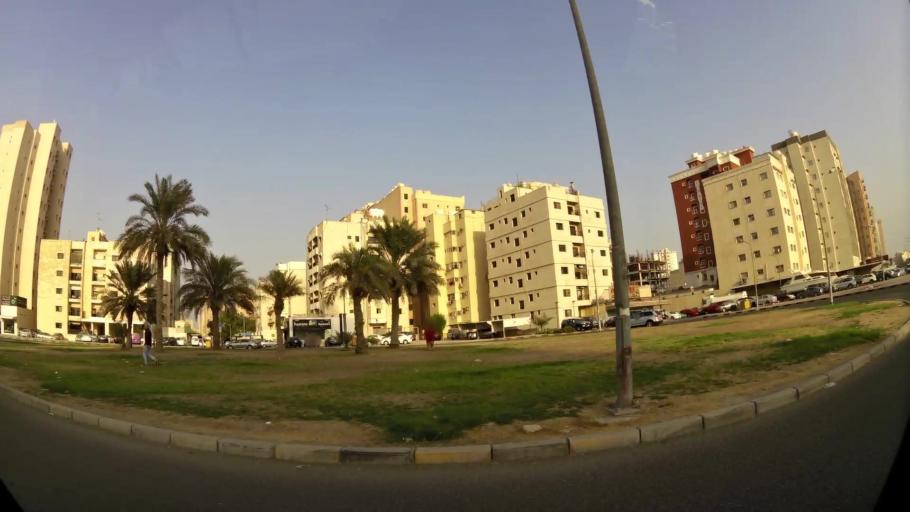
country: KW
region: Muhafazat Hawalli
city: As Salimiyah
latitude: 29.3274
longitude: 48.0672
